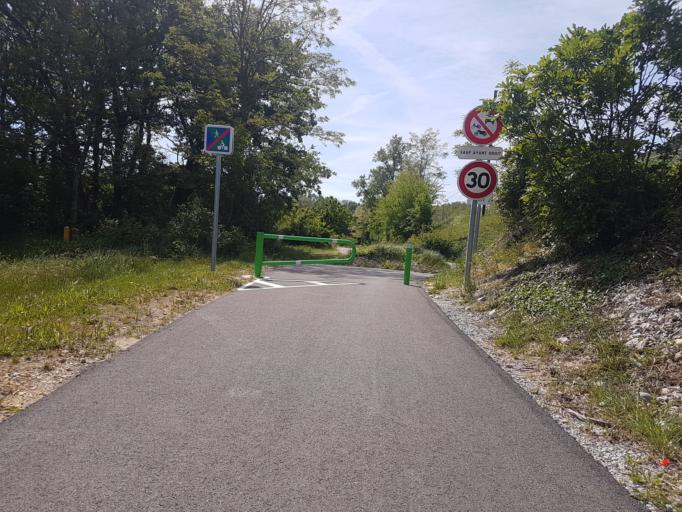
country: FR
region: Rhone-Alpes
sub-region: Departement de la Drome
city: Saulce-sur-Rhone
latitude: 44.7021
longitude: 4.7667
